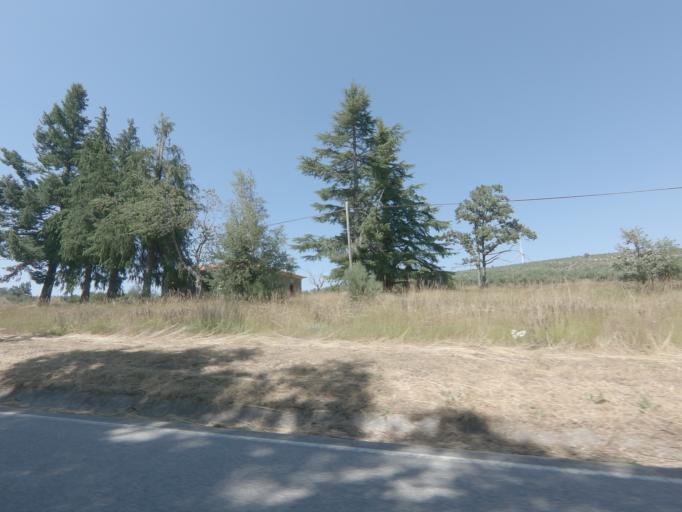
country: PT
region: Viseu
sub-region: Tarouca
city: Tarouca
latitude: 40.9871
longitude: -7.8054
